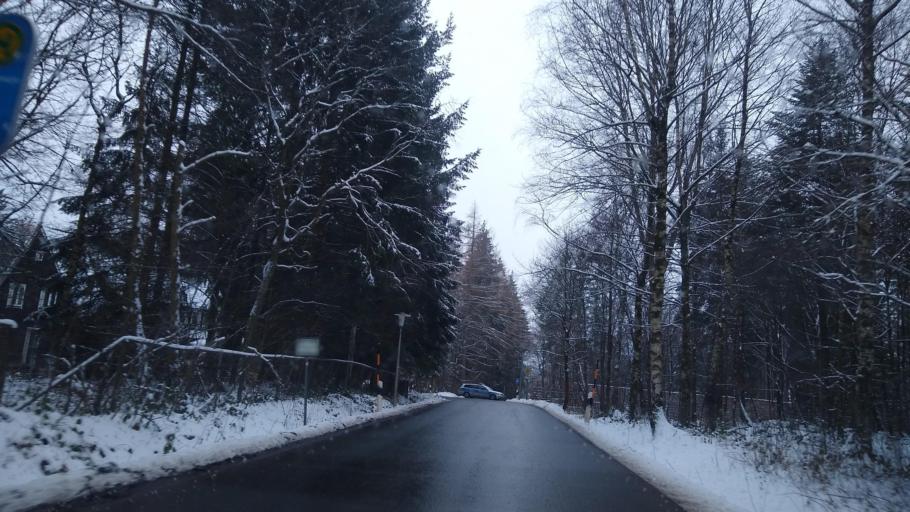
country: DE
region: Lower Saxony
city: Braunlage
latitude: 51.7304
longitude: 10.6207
